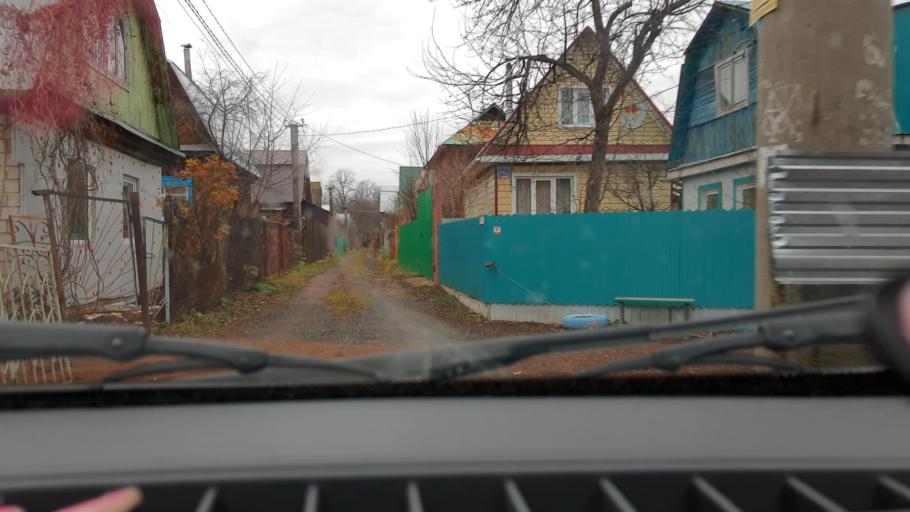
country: RU
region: Bashkortostan
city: Ufa
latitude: 54.6945
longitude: 55.8967
